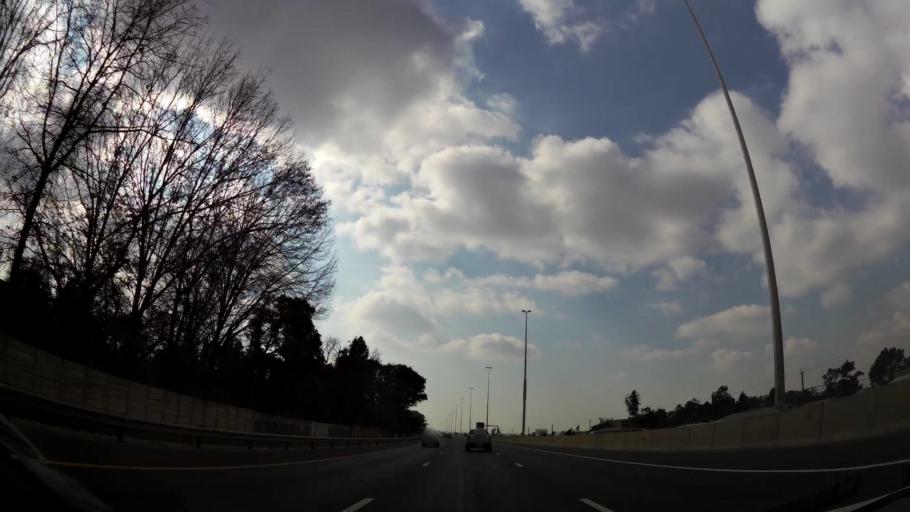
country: ZA
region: Gauteng
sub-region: Ekurhuleni Metropolitan Municipality
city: Benoni
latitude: -26.1711
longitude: 28.3476
